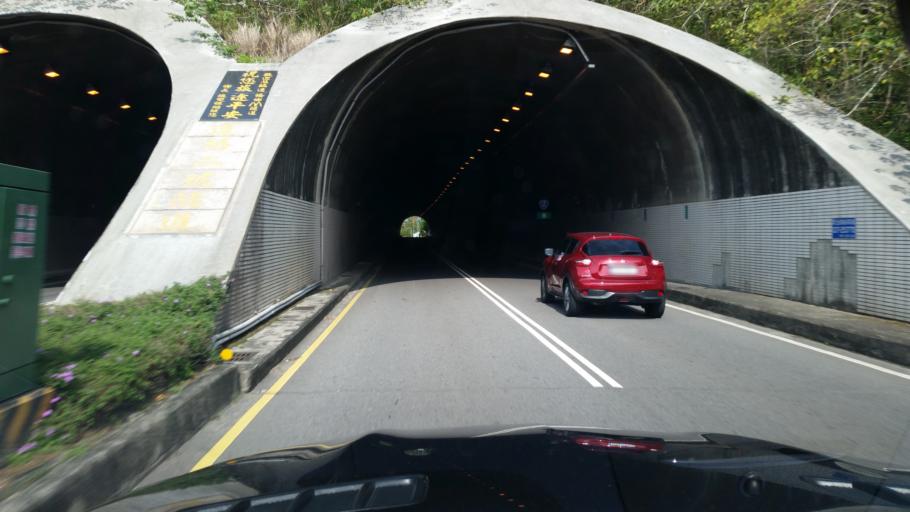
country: TW
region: Taiwan
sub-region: Miaoli
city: Miaoli
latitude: 24.6354
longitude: 120.8581
